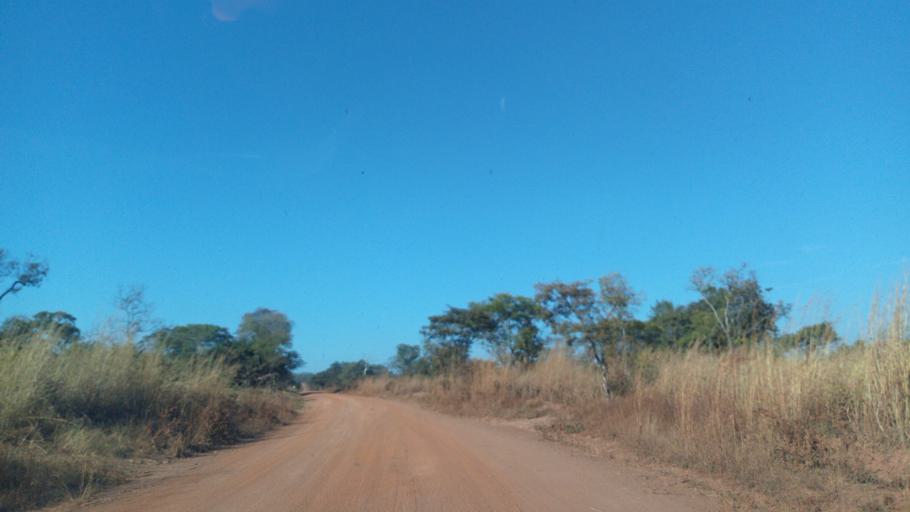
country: ZM
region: Luapula
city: Mwense
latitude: -10.5674
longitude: 28.4355
